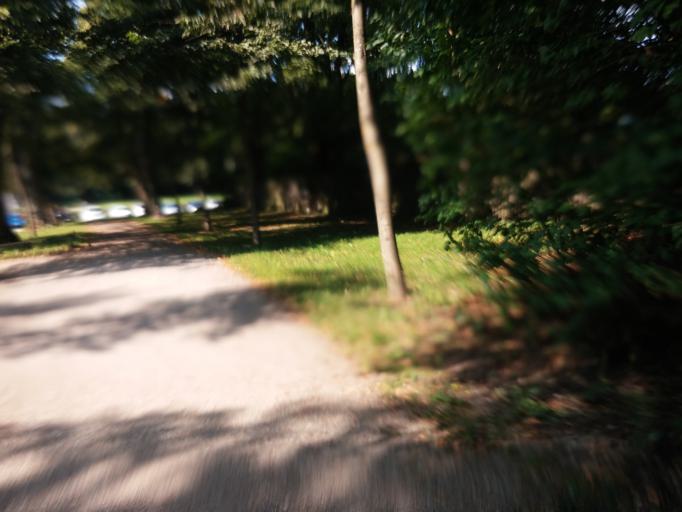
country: DE
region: Bavaria
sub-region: Upper Bavaria
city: Munich
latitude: 48.1670
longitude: 11.5686
